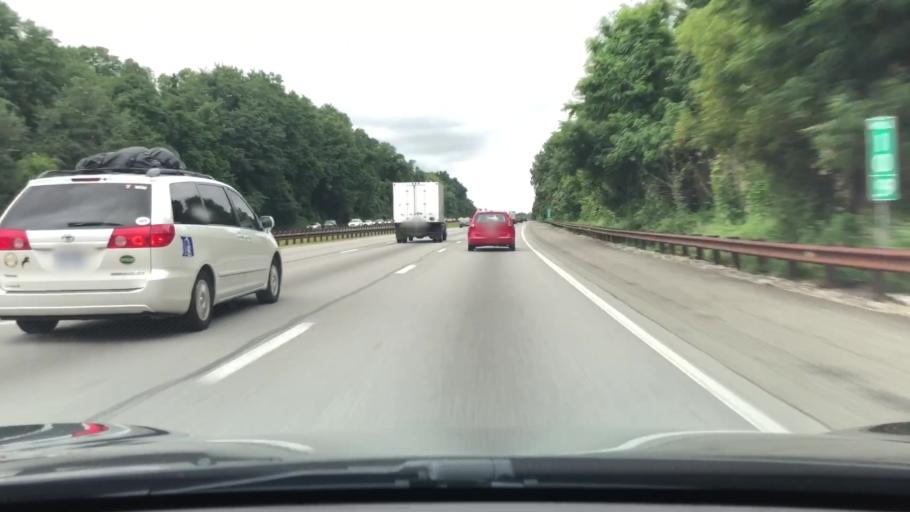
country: US
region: Pennsylvania
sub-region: Delaware County
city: Broomall
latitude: 40.0077
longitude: -75.3546
